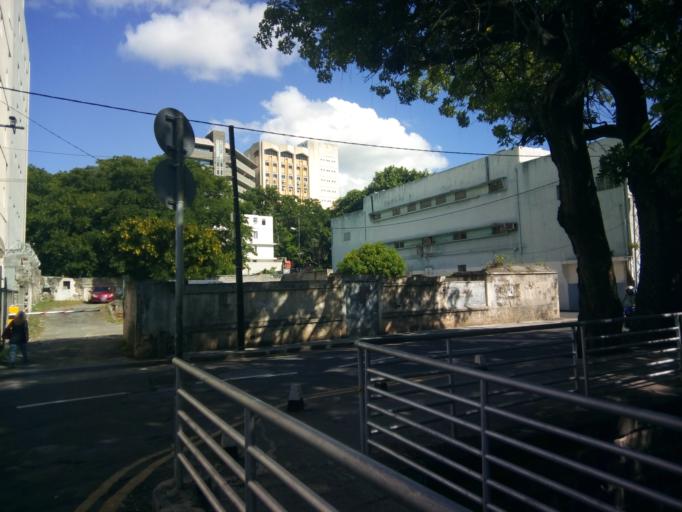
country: MU
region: Port Louis
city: Port Louis
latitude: -20.1652
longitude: 57.5038
